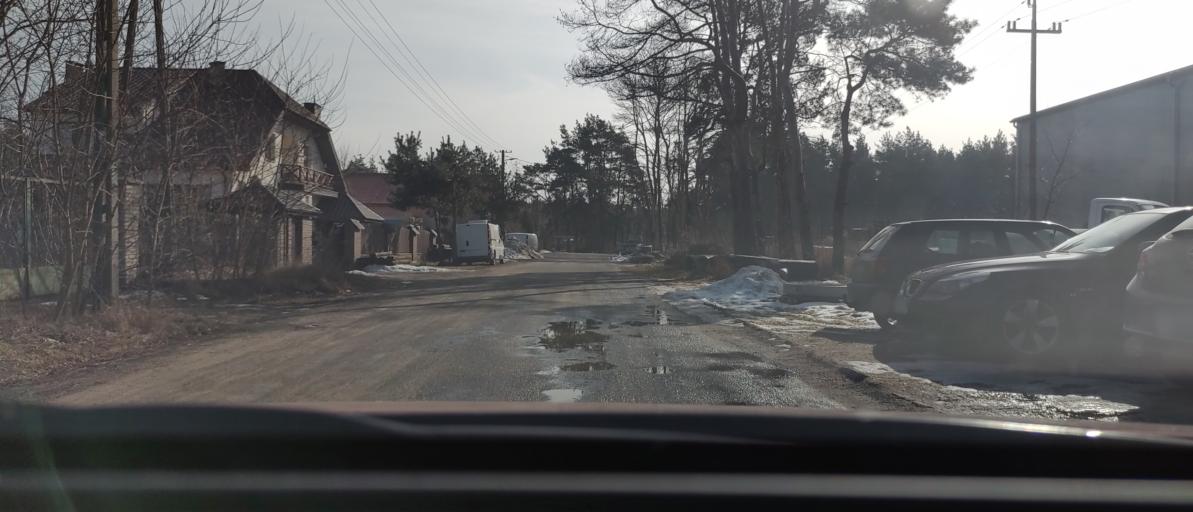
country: PL
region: Masovian Voivodeship
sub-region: Powiat bialobrzeski
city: Bialobrzegi
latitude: 51.6461
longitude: 20.9390
